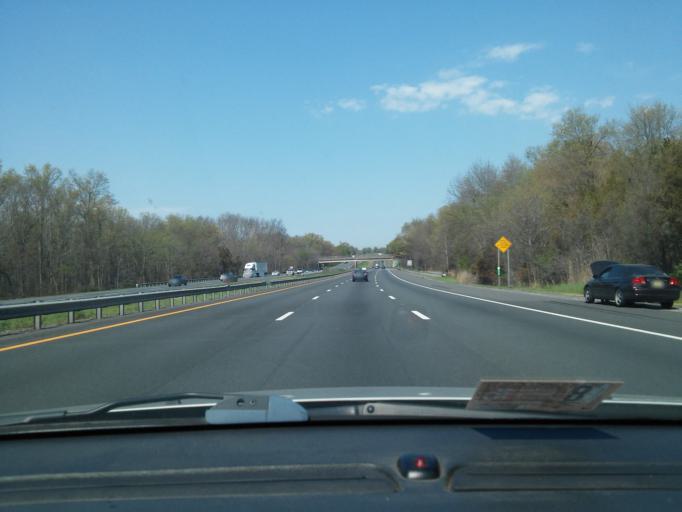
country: US
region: New Jersey
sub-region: Hunterdon County
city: Whitehouse Station
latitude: 40.6507
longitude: -74.7619
